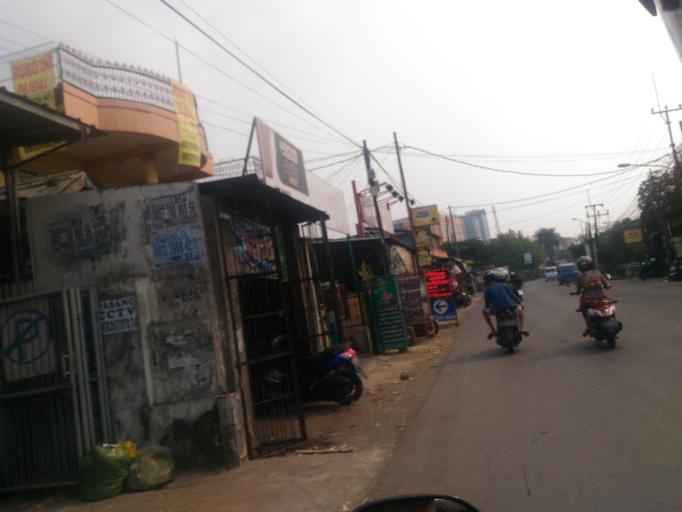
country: ID
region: West Java
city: Bogor
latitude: -6.5457
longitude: 106.8252
